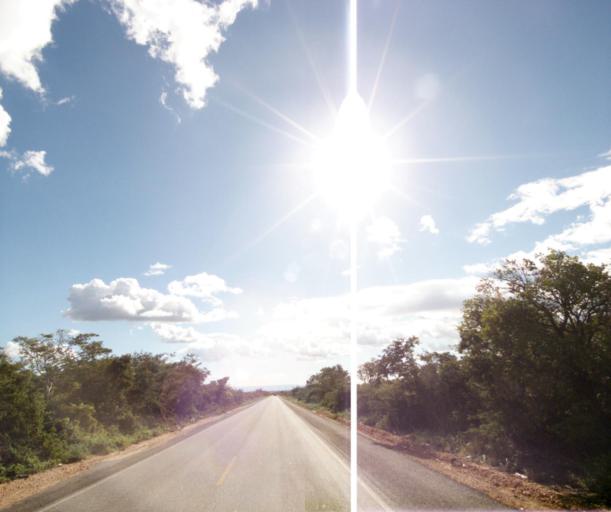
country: BR
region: Bahia
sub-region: Caetite
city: Caetite
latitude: -14.1293
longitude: -42.6264
